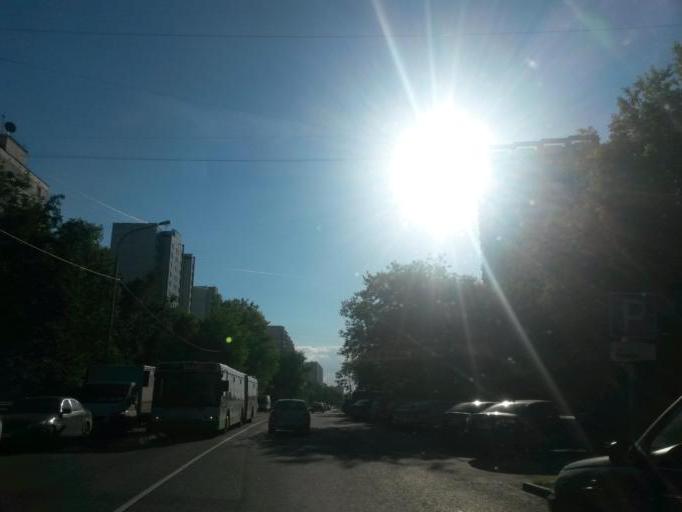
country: RU
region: Moscow
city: Zyablikovo
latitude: 55.6222
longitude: 37.7476
